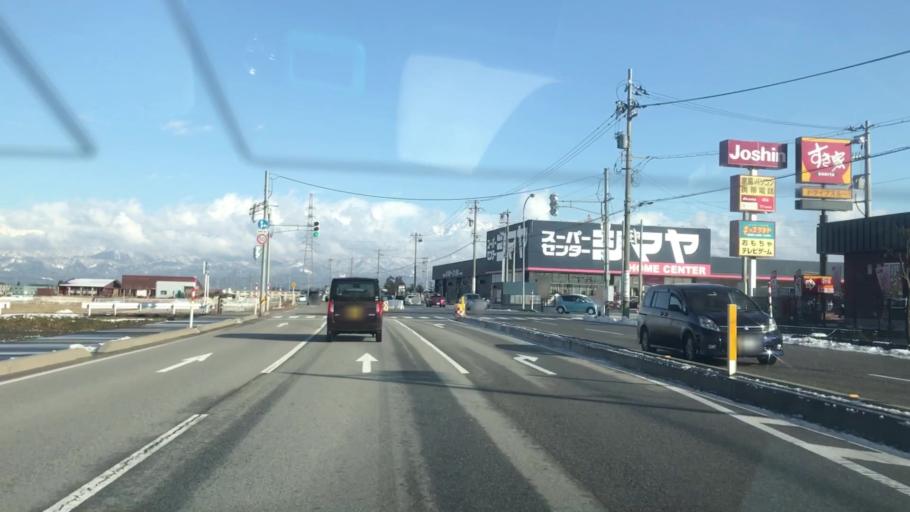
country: JP
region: Toyama
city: Kamiichi
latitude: 36.6862
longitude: 137.2933
